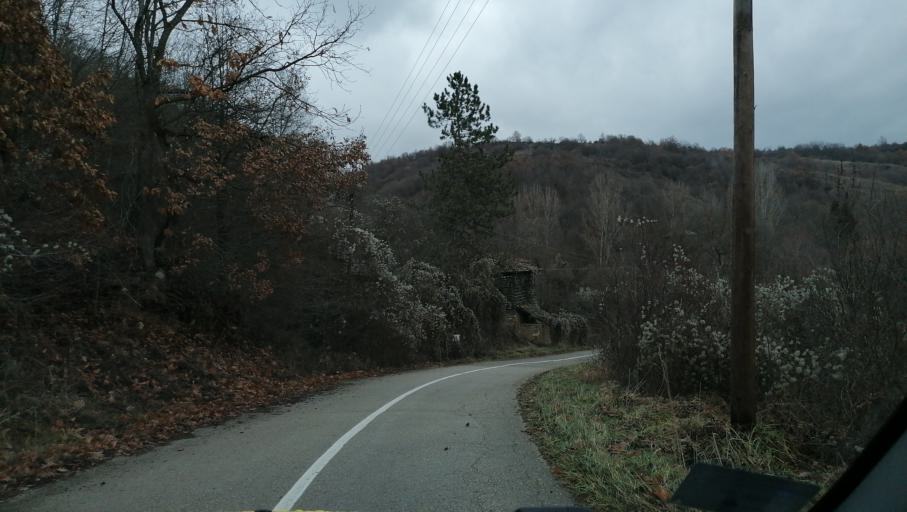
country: RS
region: Central Serbia
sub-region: Pirotski Okrug
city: Dimitrovgrad
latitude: 42.9274
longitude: 22.7566
